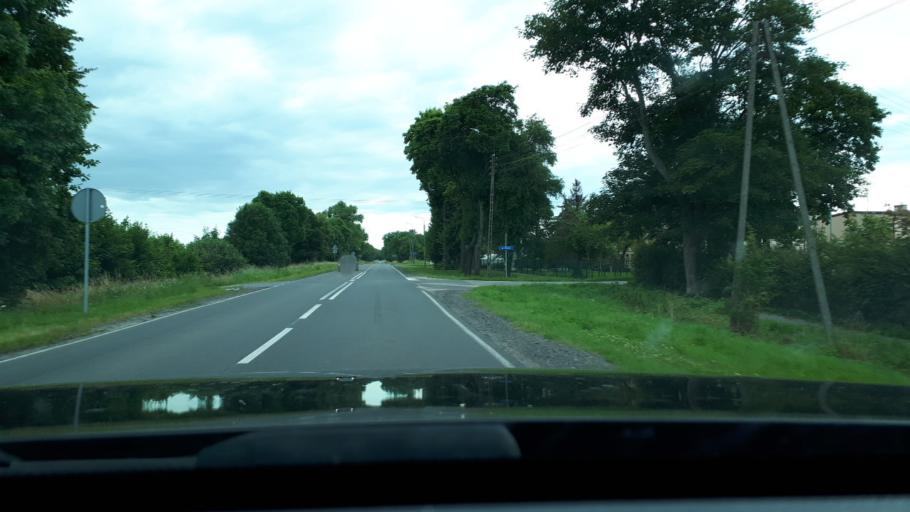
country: PL
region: Warmian-Masurian Voivodeship
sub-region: Powiat olsztynski
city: Olsztynek
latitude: 53.5738
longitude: 20.2740
